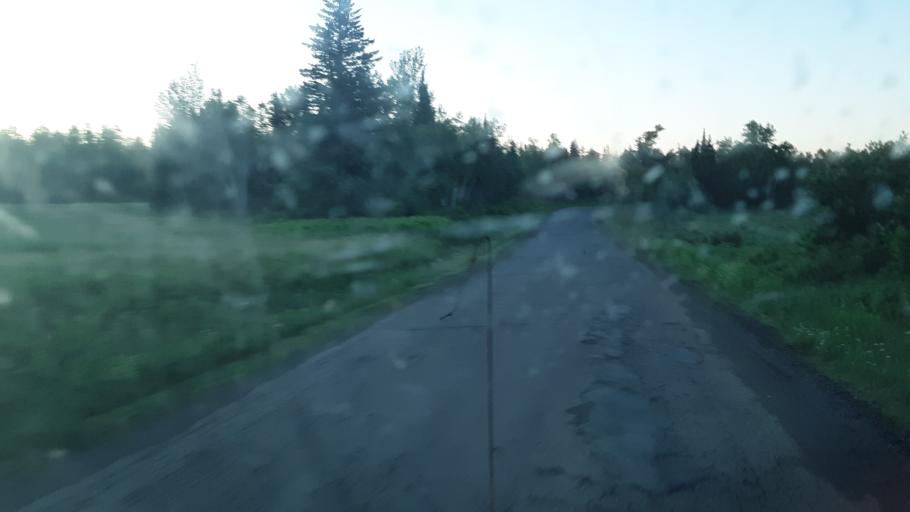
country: US
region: Maine
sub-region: Aroostook County
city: Caribou
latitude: 46.8589
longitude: -68.1349
